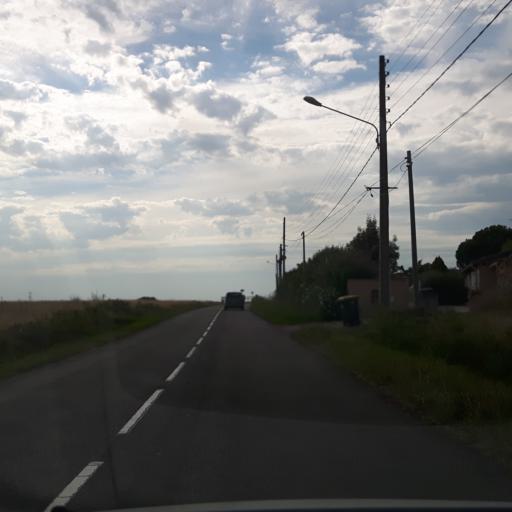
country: FR
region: Midi-Pyrenees
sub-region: Departement de la Haute-Garonne
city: Castelnau-d'Estretefonds
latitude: 43.7736
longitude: 1.3770
